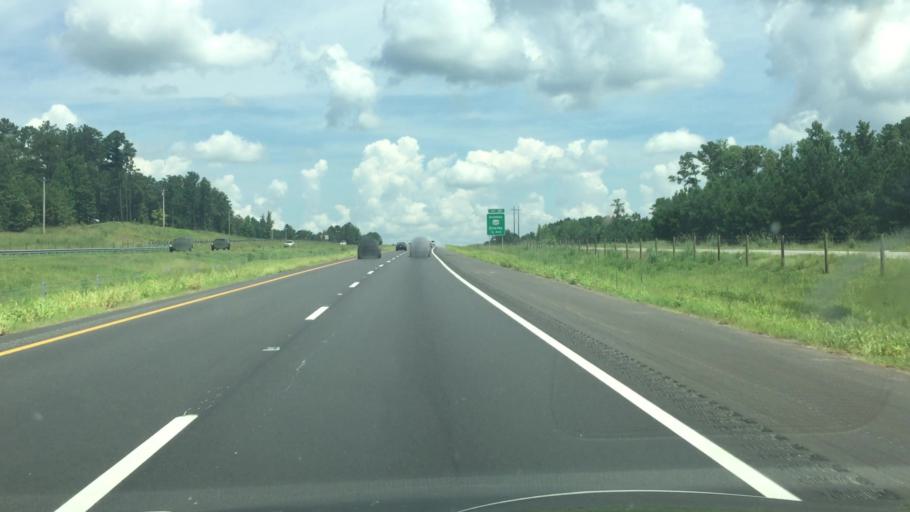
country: US
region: North Carolina
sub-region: Richmond County
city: Ellerbe
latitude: 35.0309
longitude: -79.7693
